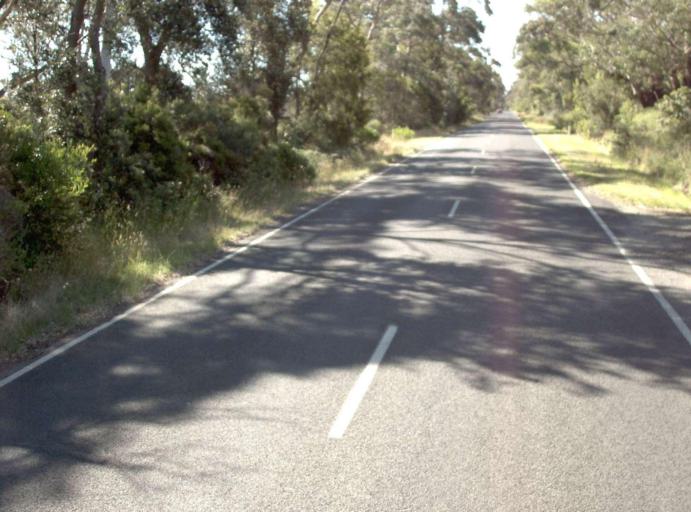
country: AU
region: Victoria
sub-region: Latrobe
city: Traralgon
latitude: -38.6636
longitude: 146.6865
